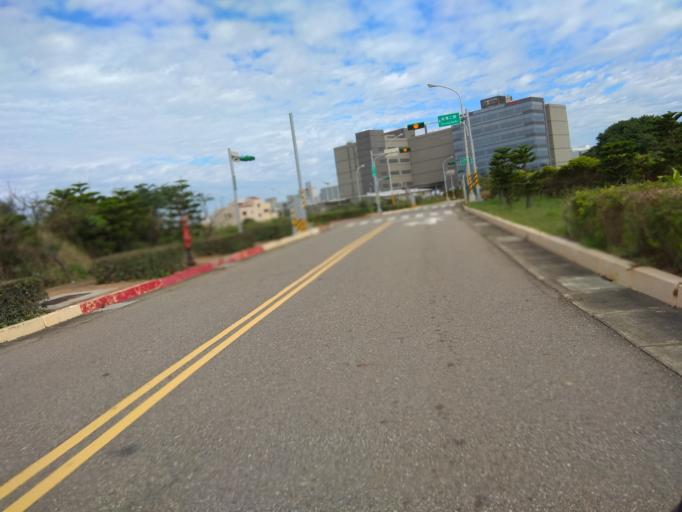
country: TW
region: Taiwan
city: Taoyuan City
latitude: 25.0464
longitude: 121.0873
